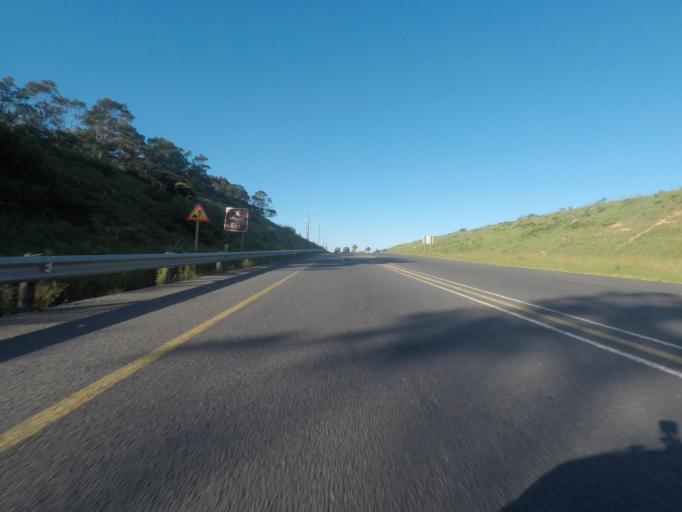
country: ZA
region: Eastern Cape
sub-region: Buffalo City Metropolitan Municipality
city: East London
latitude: -33.0417
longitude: 27.8299
